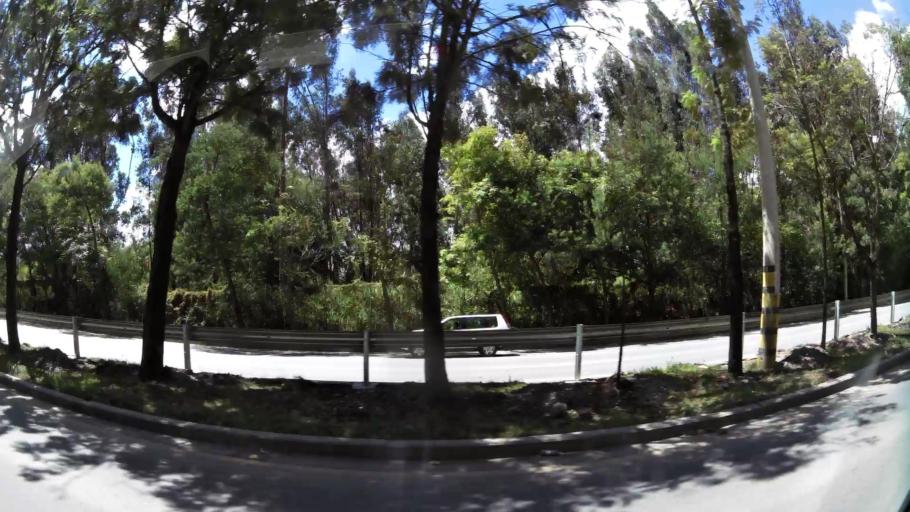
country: EC
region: Azuay
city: Llacao
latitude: -2.8763
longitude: -78.9407
